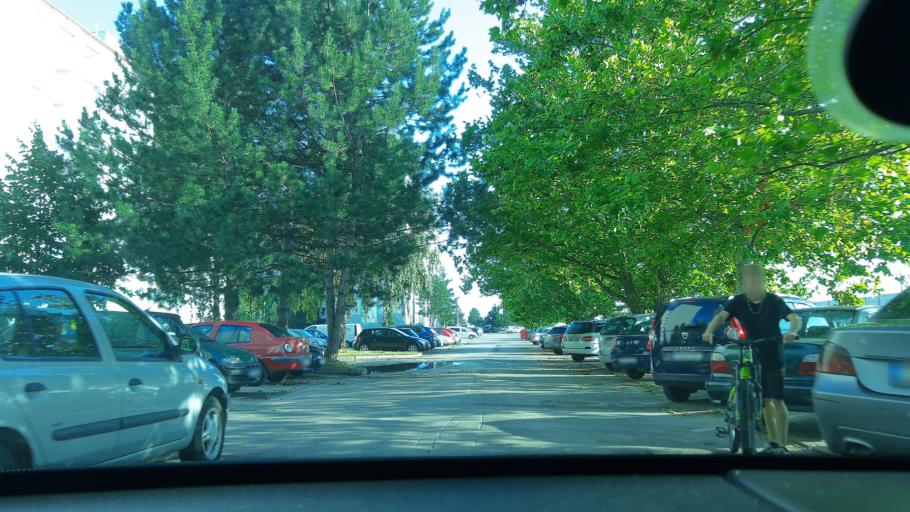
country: SK
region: Trnavsky
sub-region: Okres Trnava
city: Piestany
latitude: 48.5817
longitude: 17.8088
